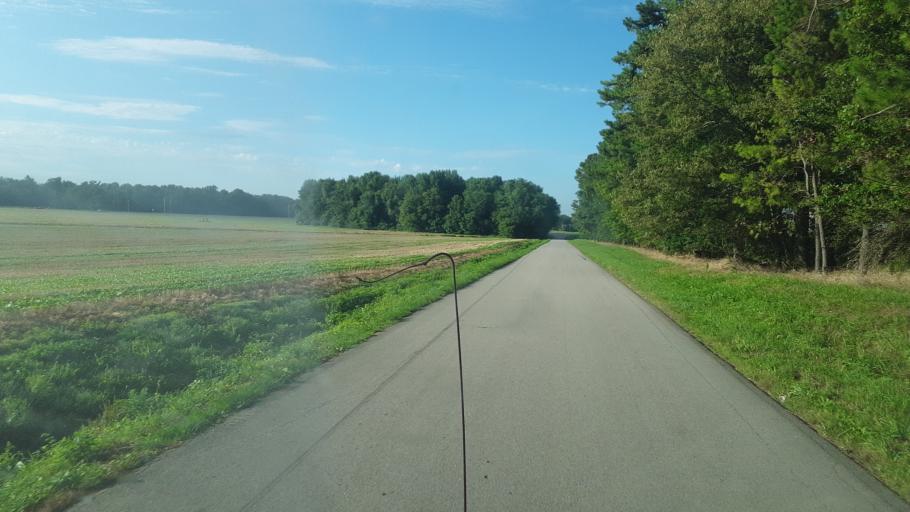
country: US
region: Kentucky
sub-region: Todd County
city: Guthrie
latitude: 36.6696
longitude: -87.1695
